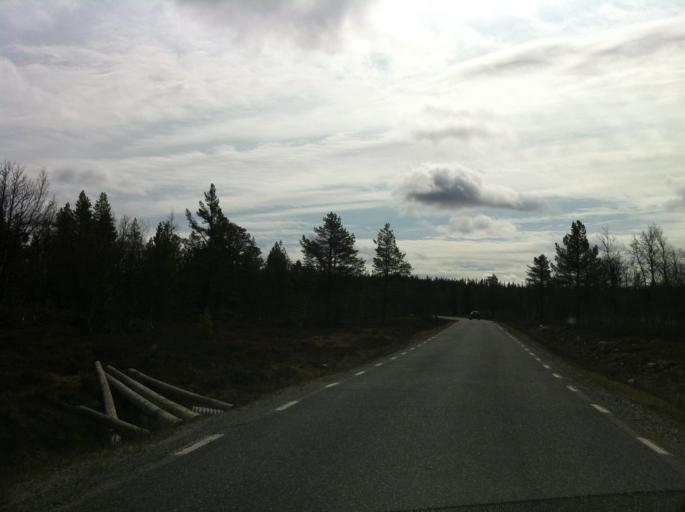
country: NO
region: Hedmark
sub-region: Engerdal
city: Engerdal
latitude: 62.3202
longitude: 12.8088
